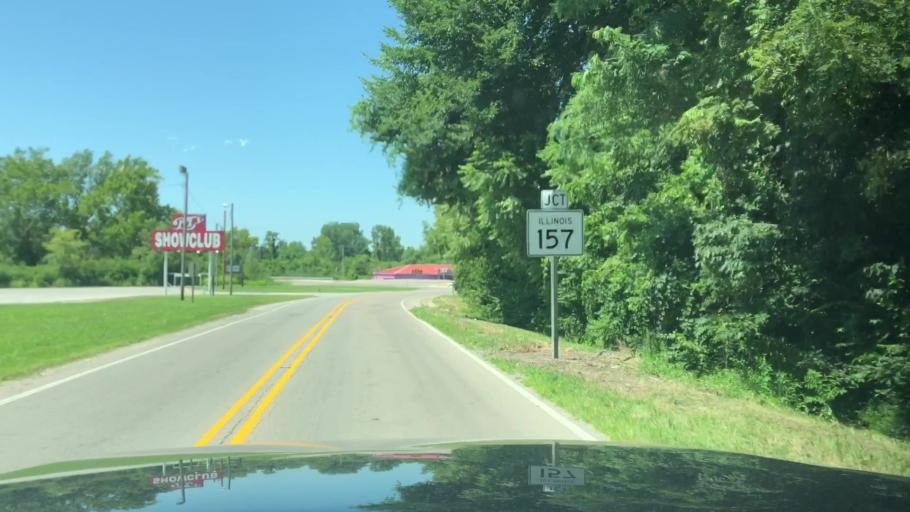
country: US
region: Illinois
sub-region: Saint Clair County
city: Centreville
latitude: 38.5570
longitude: -90.0988
